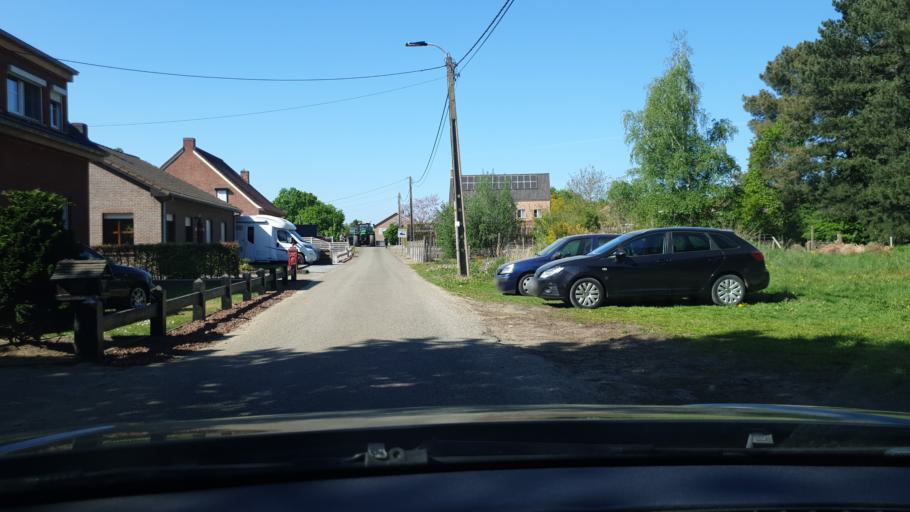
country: BE
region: Flanders
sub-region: Provincie Antwerpen
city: Laakdal
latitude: 51.1225
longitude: 5.0081
